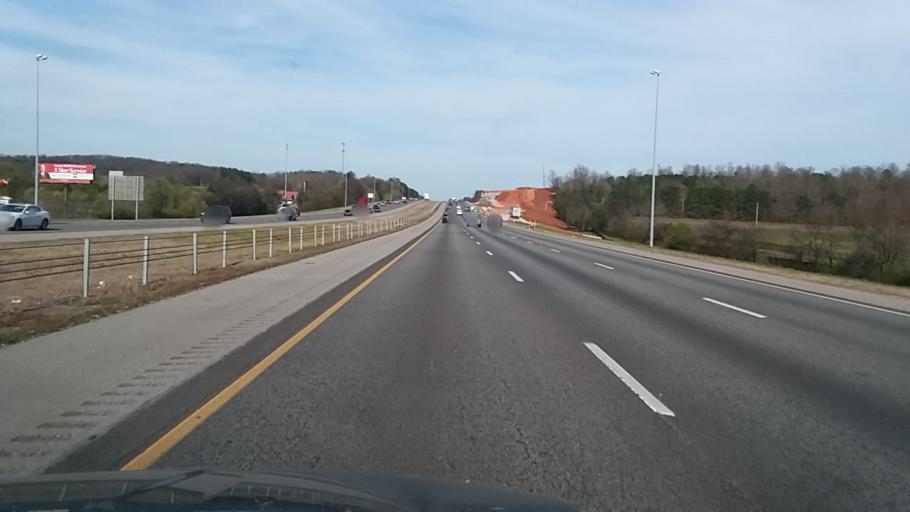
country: US
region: Alabama
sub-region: Madison County
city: Madison
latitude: 34.6797
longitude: -86.7374
